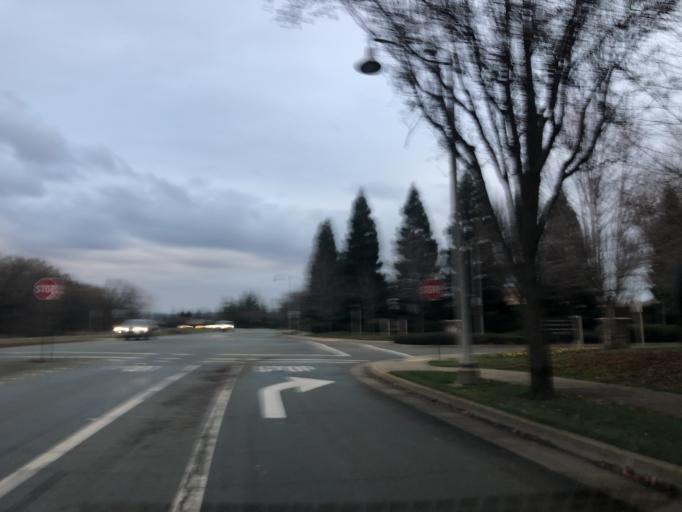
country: US
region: California
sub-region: Placer County
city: Lincoln
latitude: 38.8819
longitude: -121.2893
